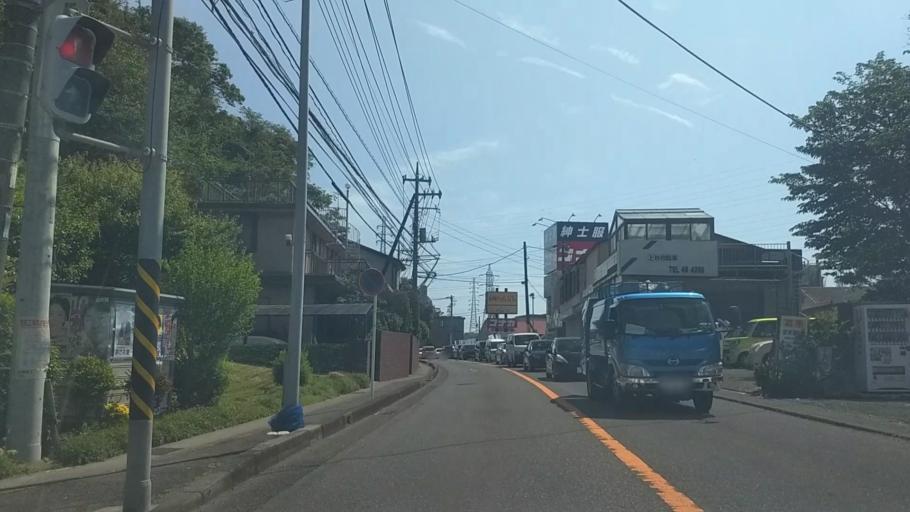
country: JP
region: Kanagawa
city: Kamakura
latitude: 35.3582
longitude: 139.5461
